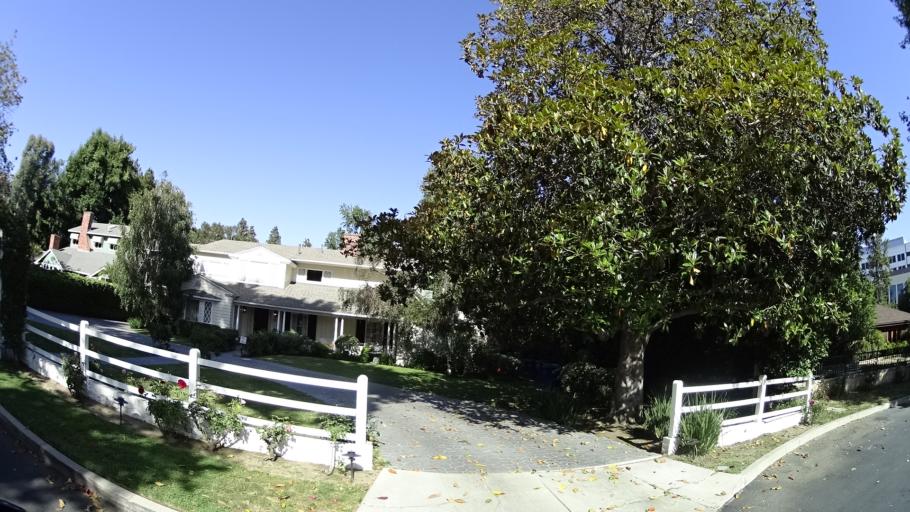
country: US
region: California
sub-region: Los Angeles County
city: Universal City
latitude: 34.1441
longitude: -118.3600
